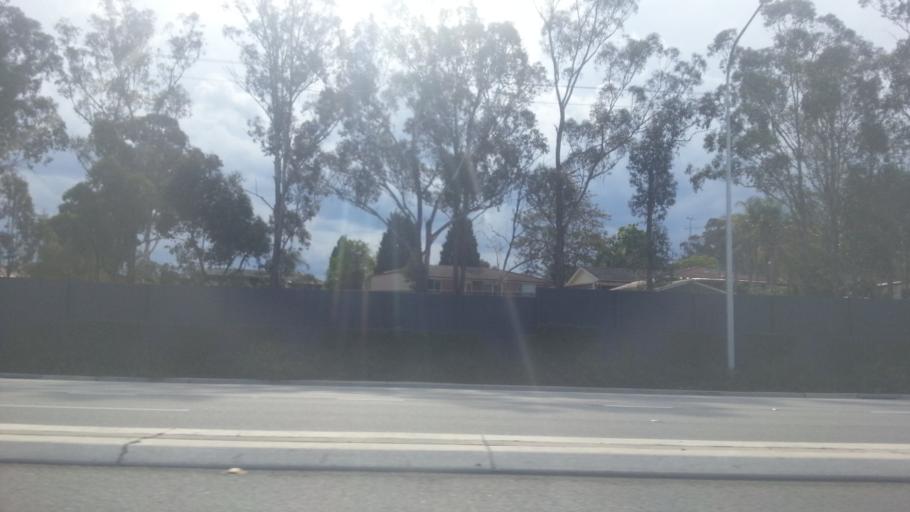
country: AU
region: New South Wales
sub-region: Penrith Municipality
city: Werrington Downs
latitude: -33.7285
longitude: 150.7200
